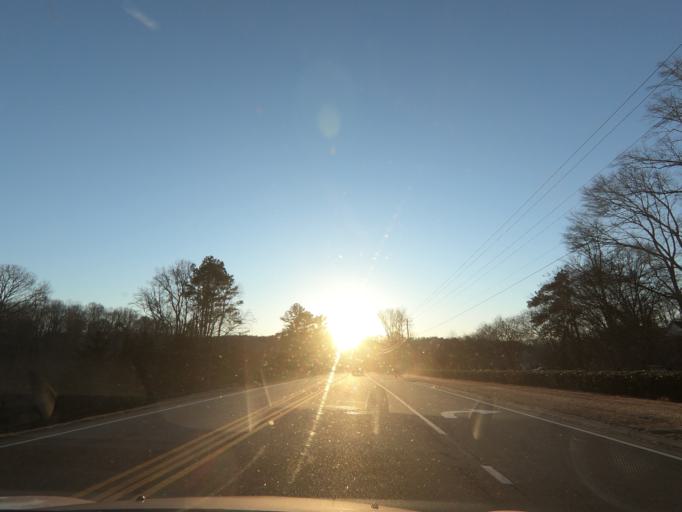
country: US
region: Georgia
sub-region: Forsyth County
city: Cumming
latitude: 34.3002
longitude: -84.2305
